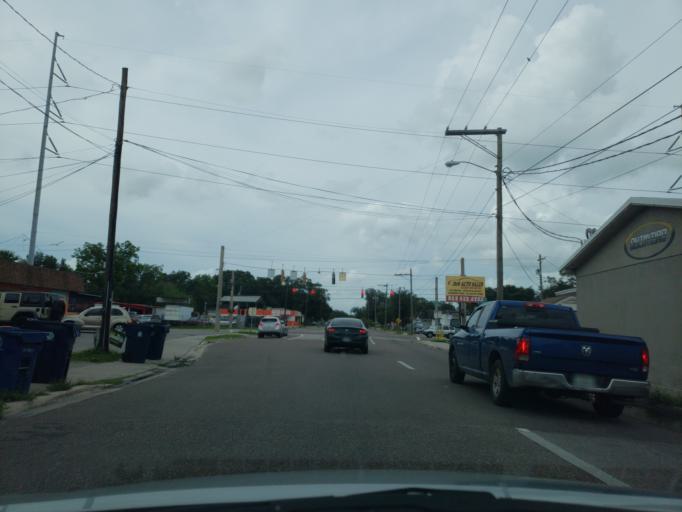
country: US
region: Florida
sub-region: Hillsborough County
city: Tampa
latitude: 27.9772
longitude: -82.4429
